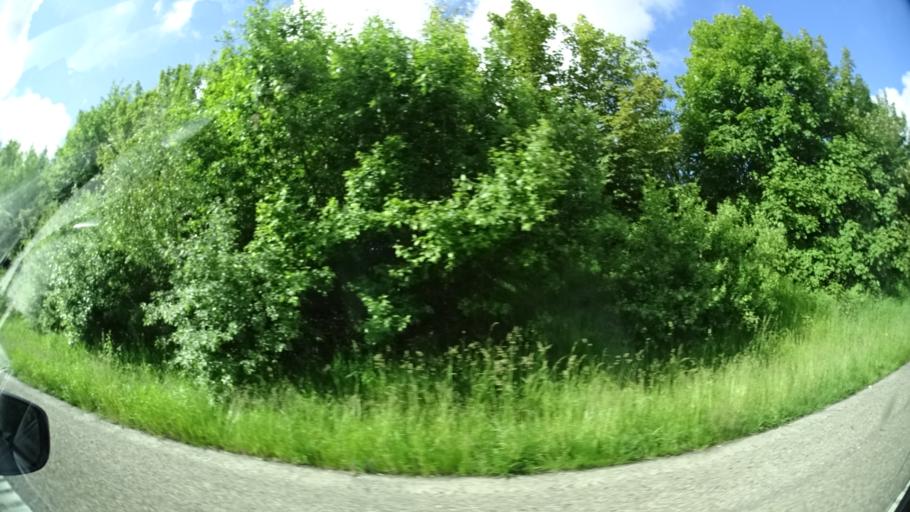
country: DK
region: Central Jutland
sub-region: Syddjurs Kommune
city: Ronde
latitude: 56.3153
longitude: 10.4888
